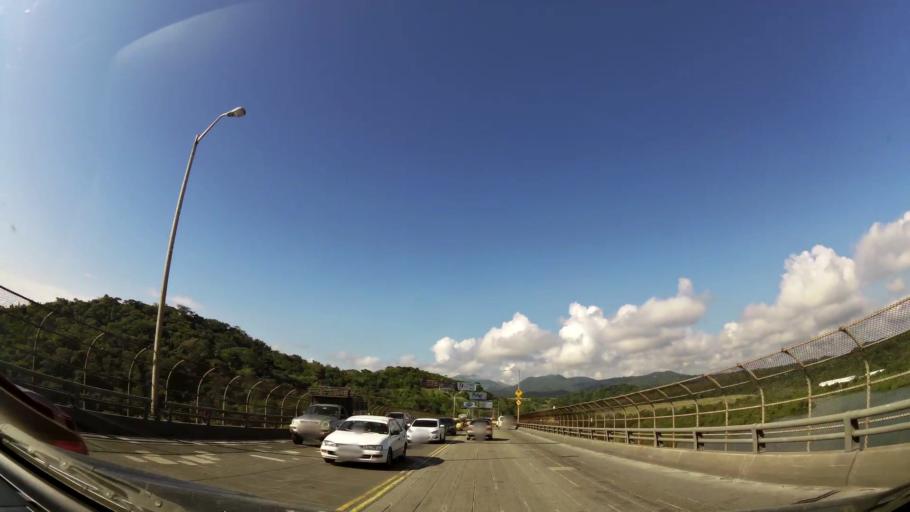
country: PA
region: Panama
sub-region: Distrito de Panama
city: Ancon
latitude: 8.9417
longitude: -79.5685
